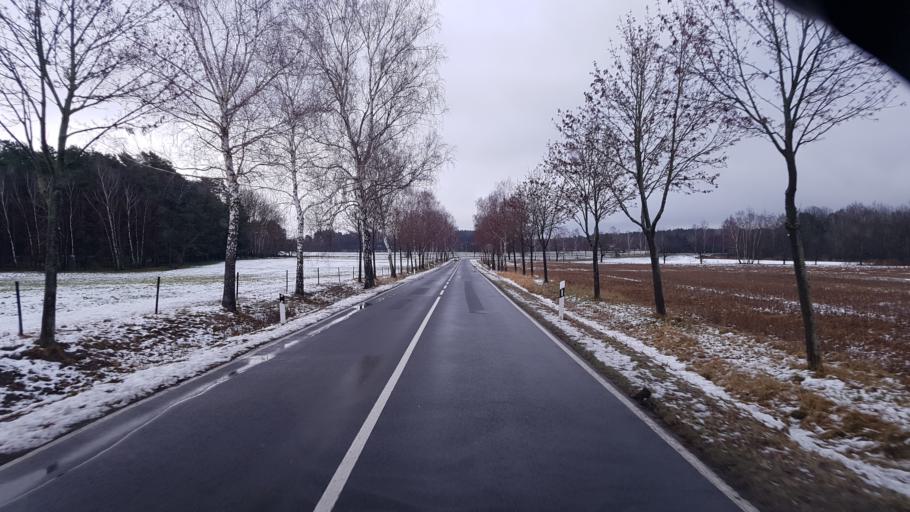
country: DE
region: Brandenburg
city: Schenkendobern
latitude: 51.9145
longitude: 14.6227
